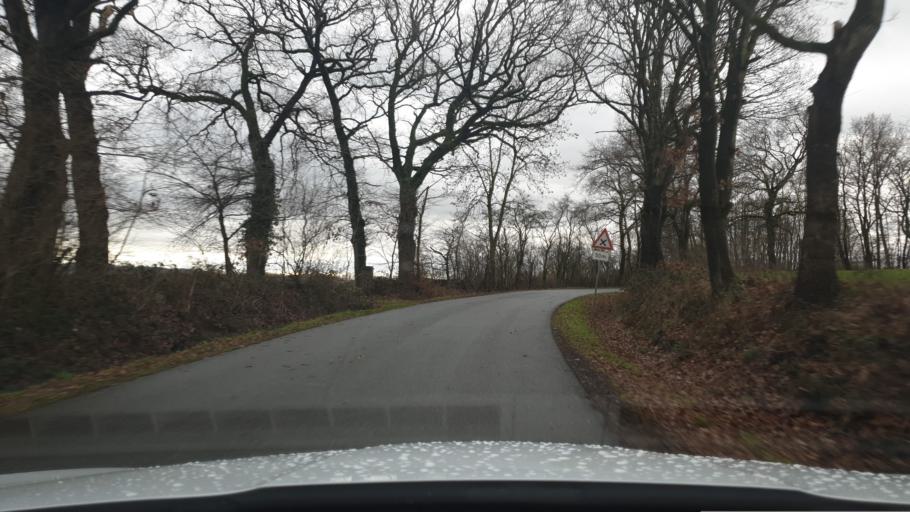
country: DE
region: North Rhine-Westphalia
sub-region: Regierungsbezirk Detmold
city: Vlotho
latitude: 52.1536
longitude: 8.8220
